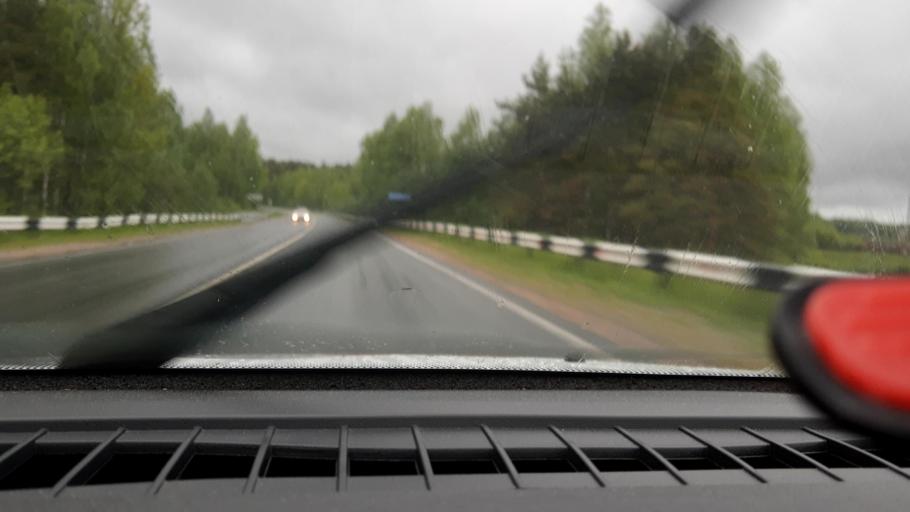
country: RU
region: Nizjnij Novgorod
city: Semenov
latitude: 56.7943
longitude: 44.4580
